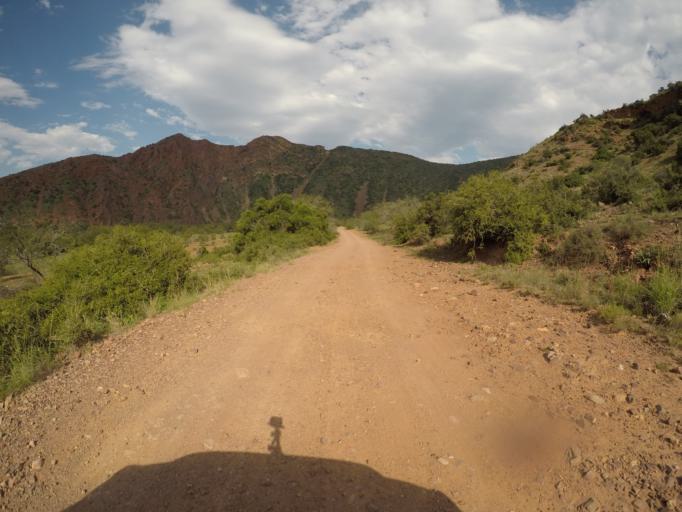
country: ZA
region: Eastern Cape
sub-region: Cacadu District Municipality
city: Kareedouw
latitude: -33.6389
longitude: 24.3167
